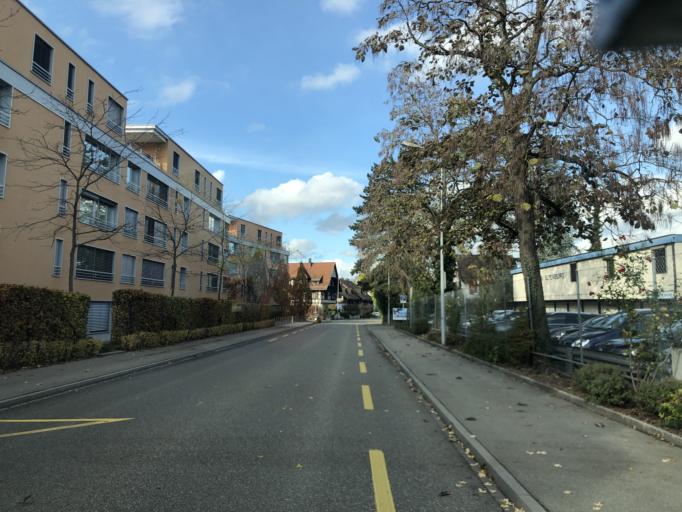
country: CH
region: Aargau
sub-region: Bezirk Baden
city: Wettingen
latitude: 47.4635
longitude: 8.3132
